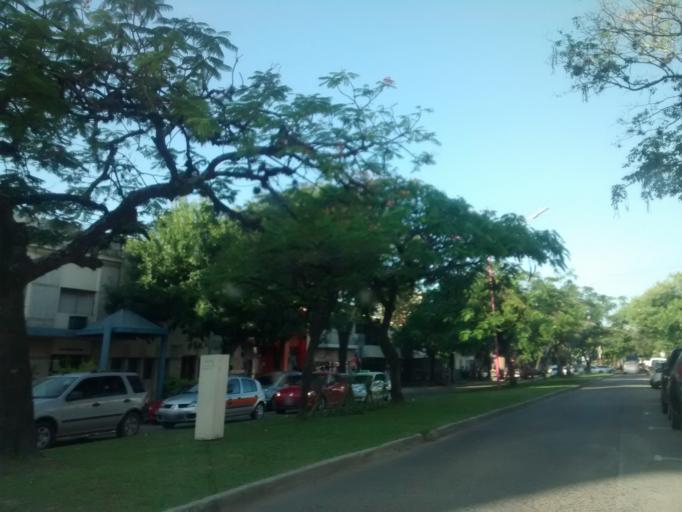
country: AR
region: Chaco
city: Resistencia
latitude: -27.4566
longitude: -58.9837
